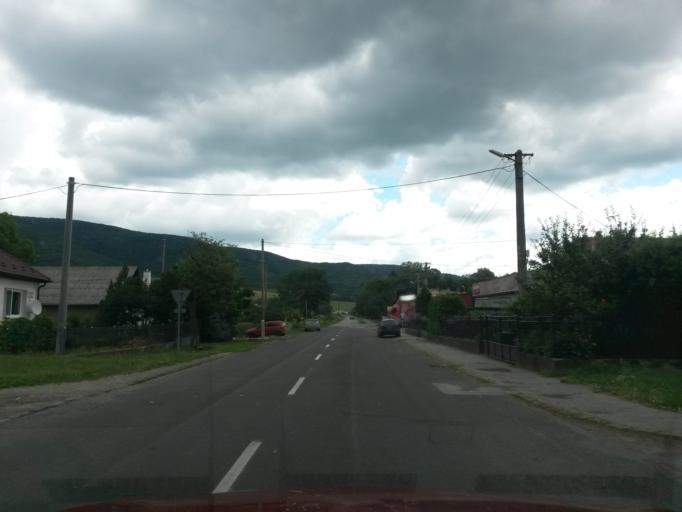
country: SK
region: Kosicky
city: Strazske
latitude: 48.8757
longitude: 21.8412
